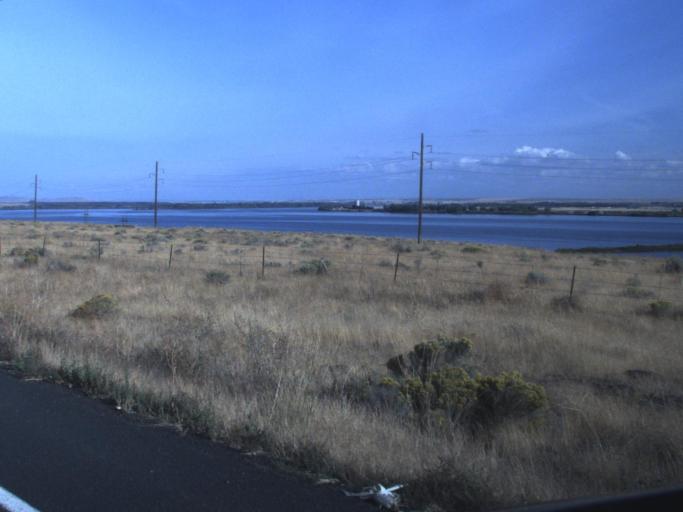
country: US
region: Oregon
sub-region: Morrow County
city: Boardman
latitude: 45.9263
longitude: -119.6299
